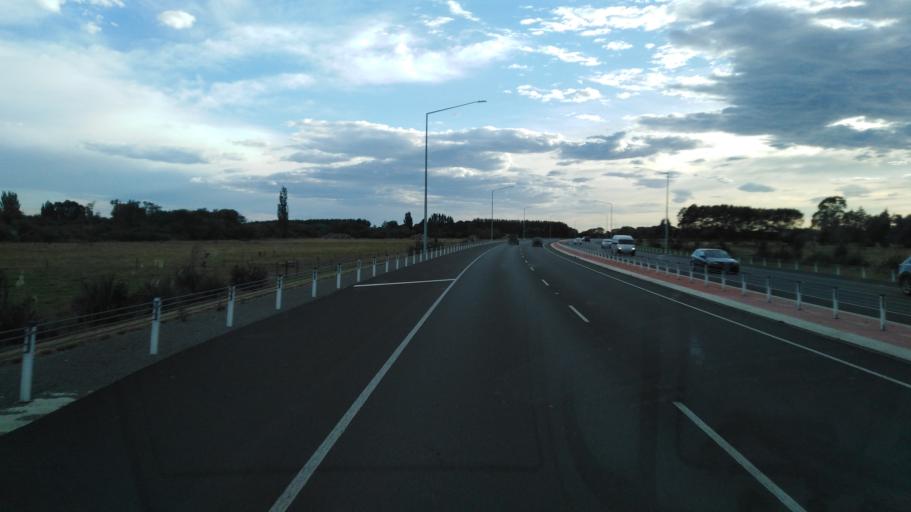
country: NZ
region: Canterbury
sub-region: Waimakariri District
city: Kaiapoi
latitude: -43.4414
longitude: 172.6193
